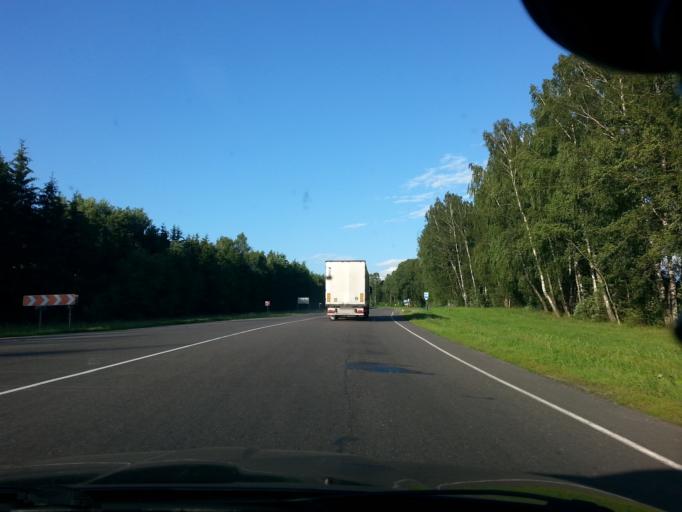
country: BY
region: Minsk
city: Svir
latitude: 54.8921
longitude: 26.3896
